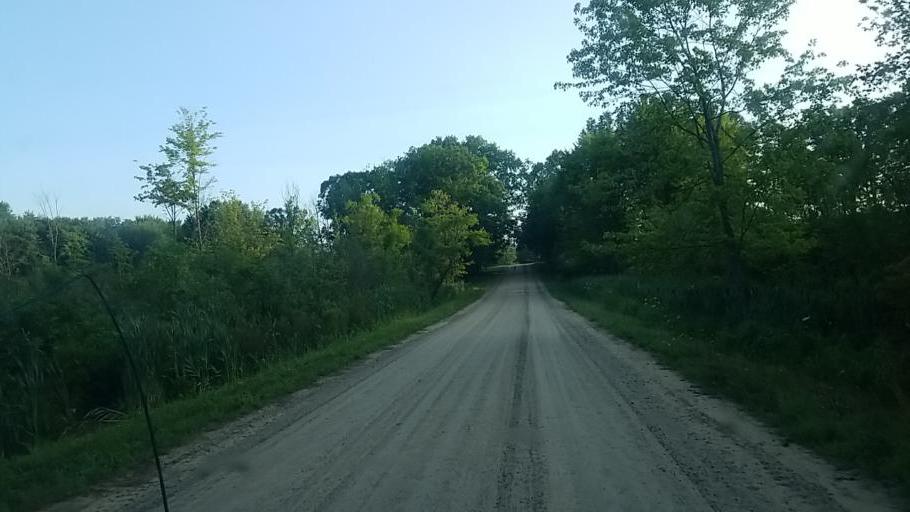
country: US
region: Michigan
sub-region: Muskegon County
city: Twin Lake
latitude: 43.4450
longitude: -86.0991
